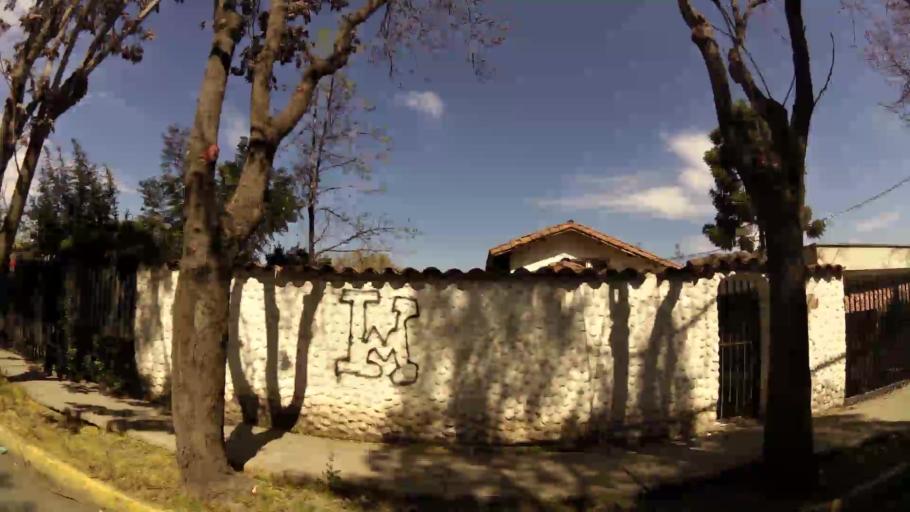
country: CL
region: Santiago Metropolitan
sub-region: Provincia de Santiago
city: Villa Presidente Frei, Nunoa, Santiago, Chile
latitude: -33.4468
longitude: -70.5296
